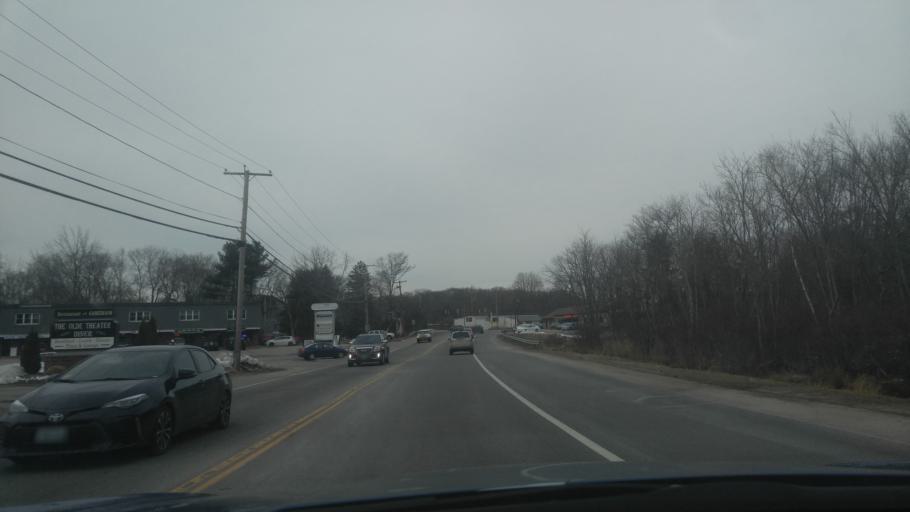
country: US
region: Rhode Island
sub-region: Kent County
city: West Warwick
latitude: 41.6887
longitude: -71.5607
